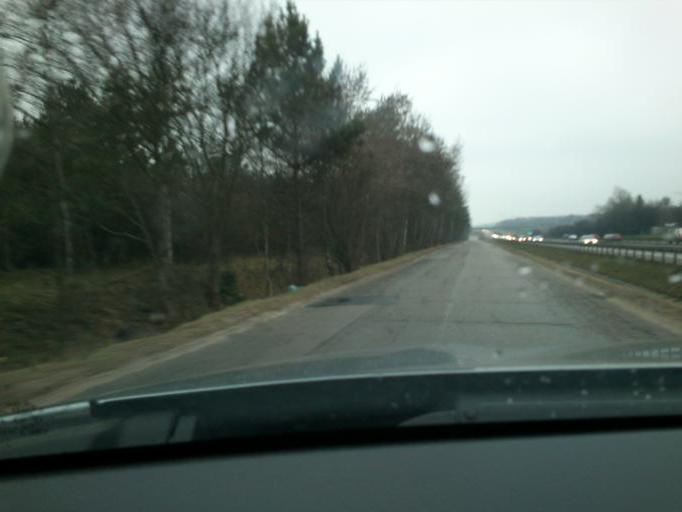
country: PL
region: Pomeranian Voivodeship
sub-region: Gdynia
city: Wielki Kack
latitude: 54.4058
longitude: 18.4853
